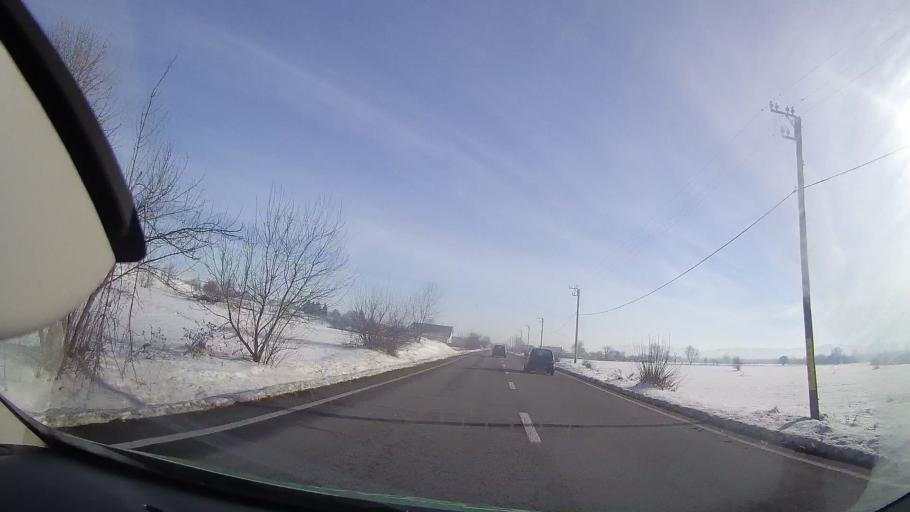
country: RO
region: Neamt
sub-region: Comuna Ghindaoani
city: Ghindaoani
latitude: 47.0816
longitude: 26.3427
